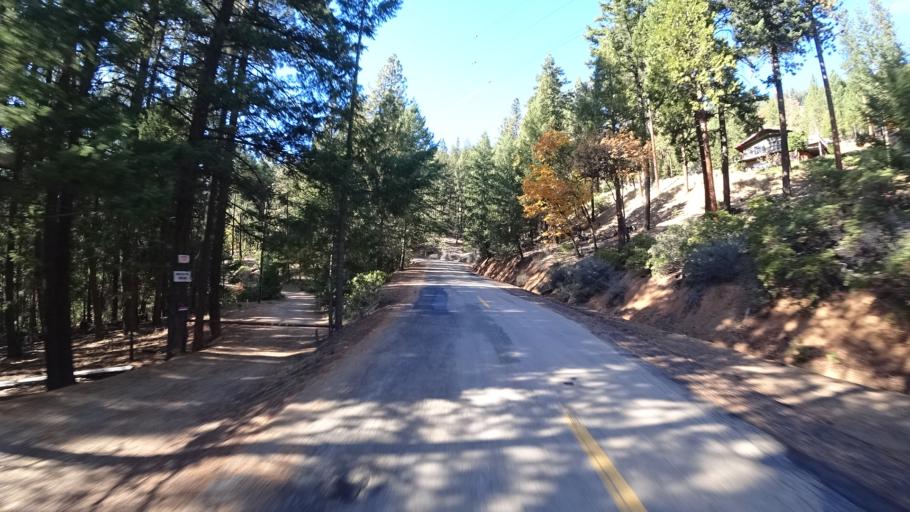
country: US
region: California
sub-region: Siskiyou County
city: Yreka
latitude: 41.7296
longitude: -122.7183
